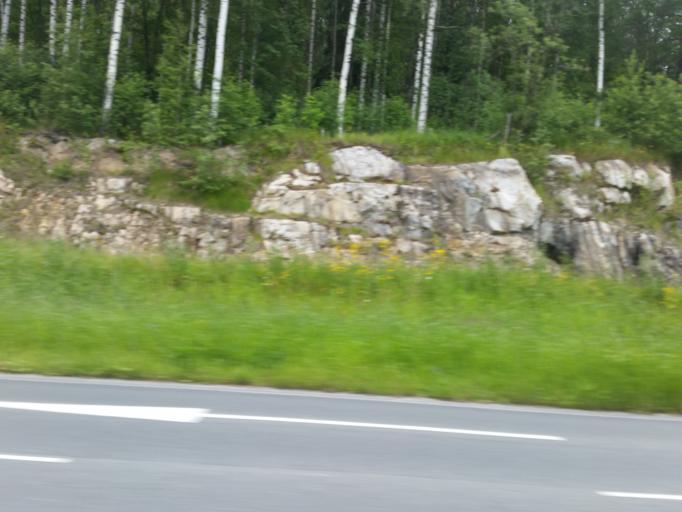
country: FI
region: Northern Savo
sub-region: Kuopio
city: Kuopio
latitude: 62.8832
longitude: 27.6461
